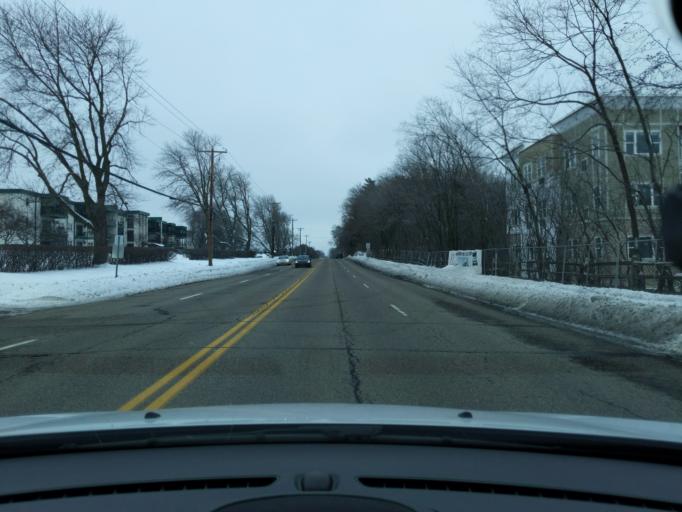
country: US
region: Minnesota
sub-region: Ramsey County
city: Roseville
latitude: 45.0207
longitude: -93.1257
